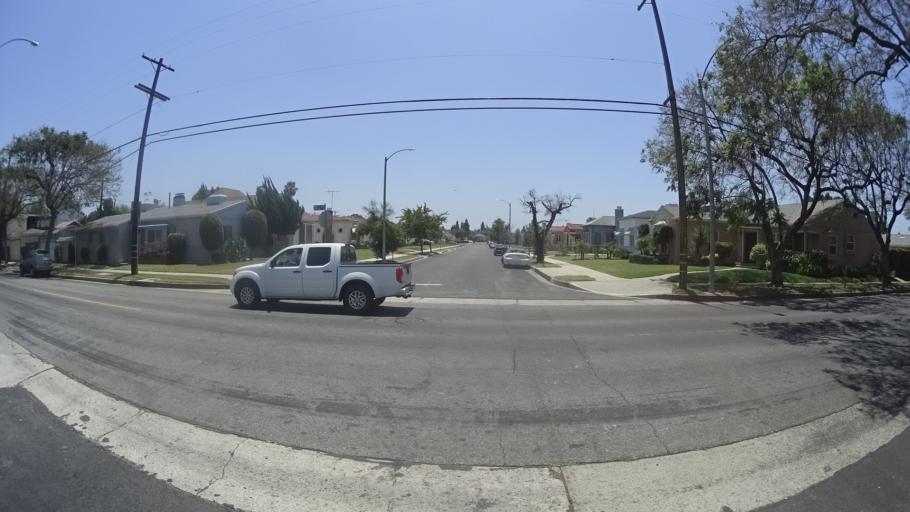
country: US
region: California
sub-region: Los Angeles County
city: View Park-Windsor Hills
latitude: 34.0147
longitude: -118.3263
